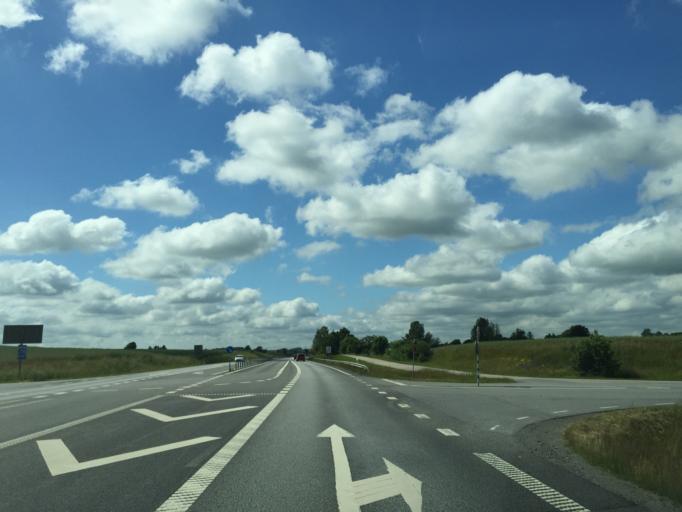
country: SE
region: Skane
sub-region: Skurups Kommun
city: Rydsgard
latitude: 55.4879
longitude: 13.5513
